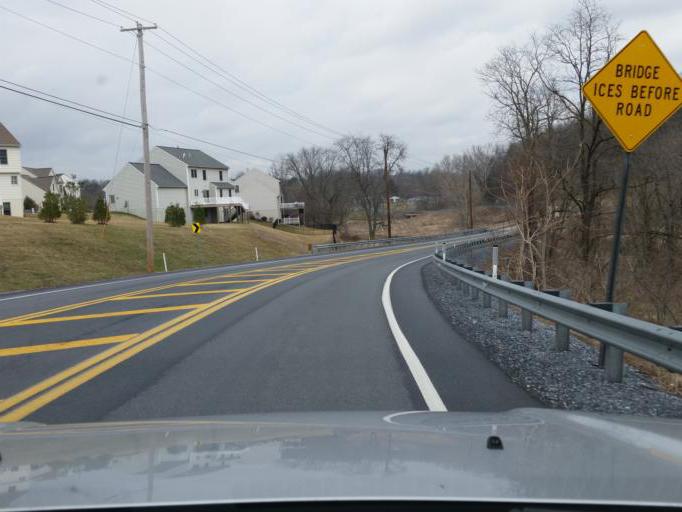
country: US
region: Pennsylvania
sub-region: Dauphin County
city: Rutherford
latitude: 40.2749
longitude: -76.7489
